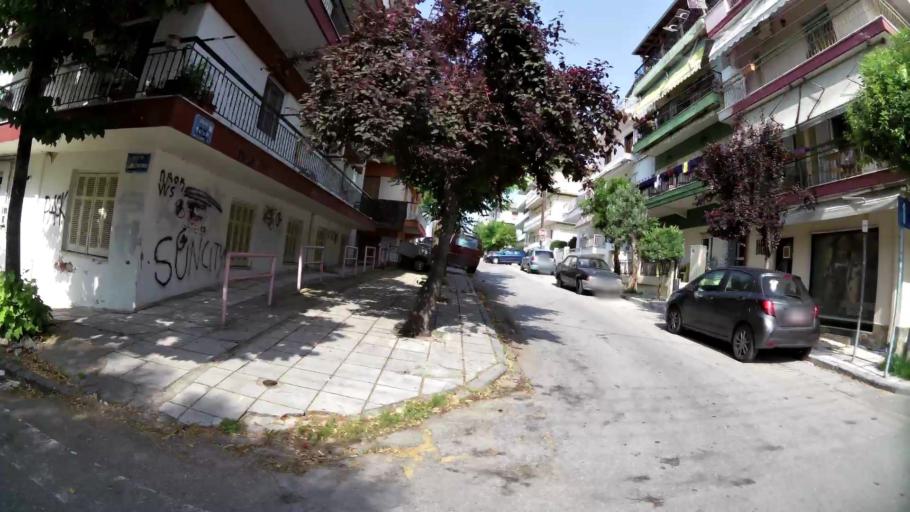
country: GR
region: Central Macedonia
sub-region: Nomos Thessalonikis
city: Stavroupoli
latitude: 40.6688
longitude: 22.9278
